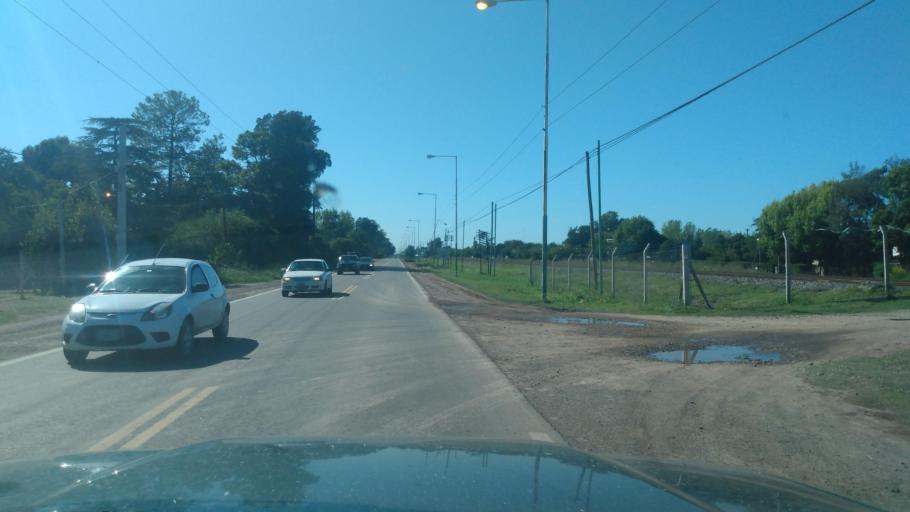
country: AR
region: Buenos Aires
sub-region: Partido de General Rodriguez
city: General Rodriguez
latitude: -34.5963
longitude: -59.0058
